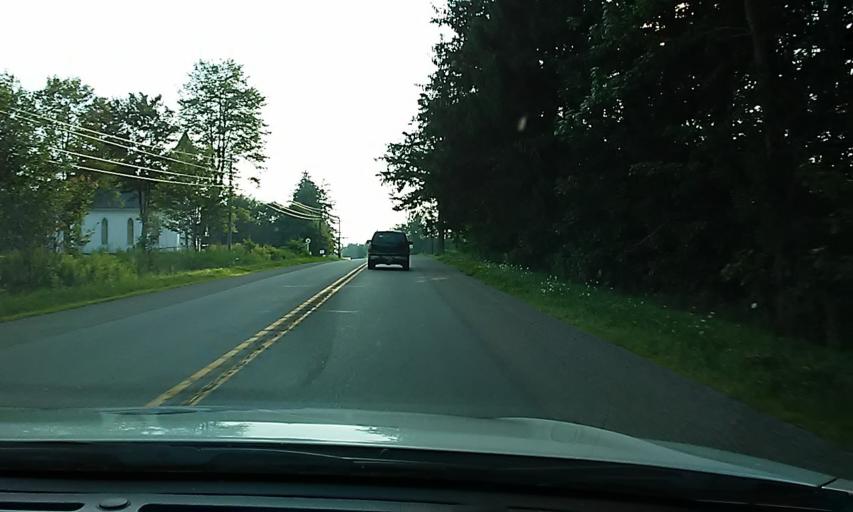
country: US
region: Pennsylvania
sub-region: McKean County
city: Kane
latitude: 41.6712
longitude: -78.7358
